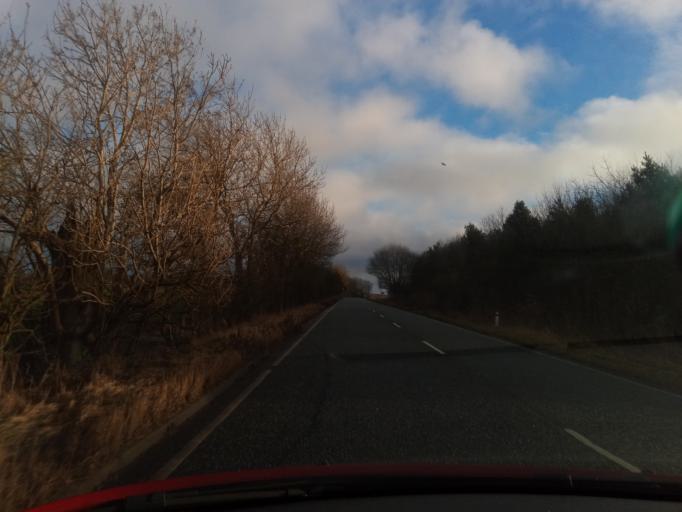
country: GB
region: England
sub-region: Northumberland
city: Rothley
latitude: 55.1385
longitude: -1.9731
